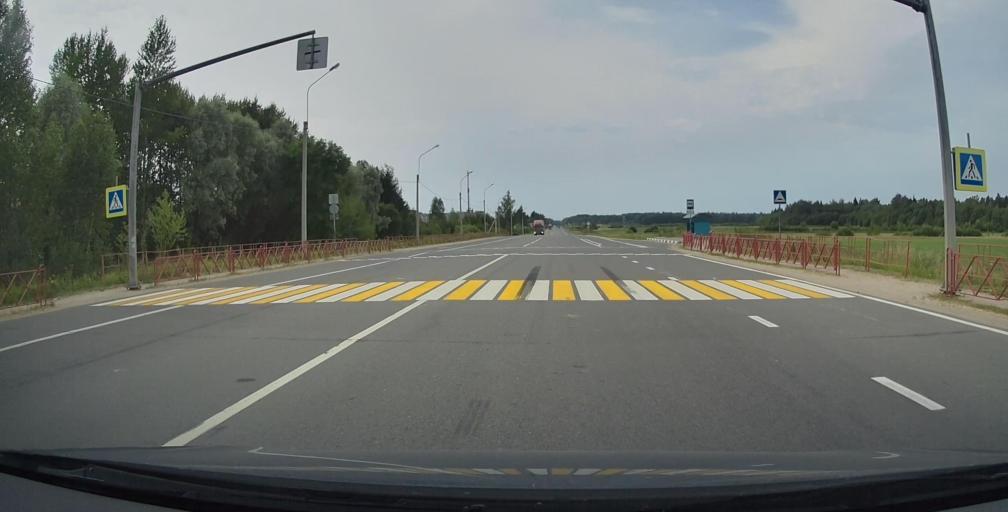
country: RU
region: Jaroslavl
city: Pesochnoye
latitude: 57.9868
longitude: 39.1139
